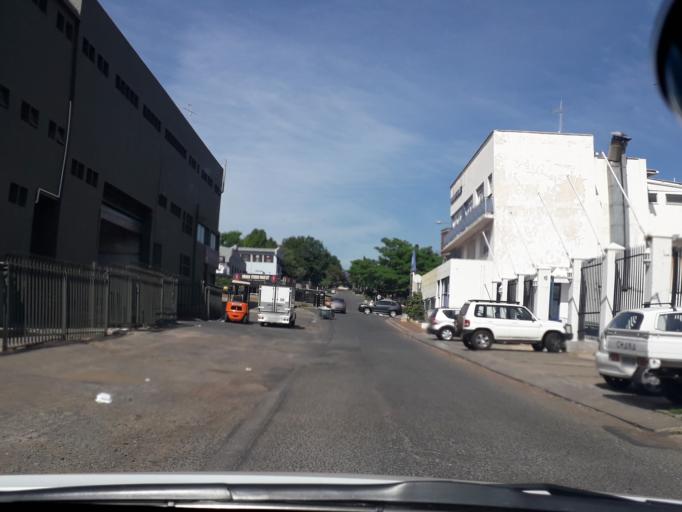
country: ZA
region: Gauteng
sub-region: City of Johannesburg Metropolitan Municipality
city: Johannesburg
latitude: -26.1358
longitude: 27.9764
